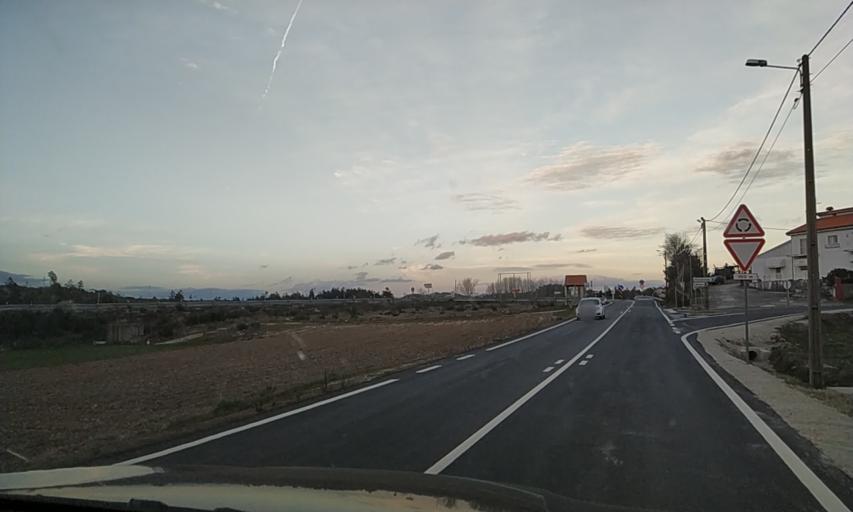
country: PT
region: Braganca
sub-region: Carrazeda de Ansiaes
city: Carrazeda de Anciaes
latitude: 41.2516
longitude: -7.2856
